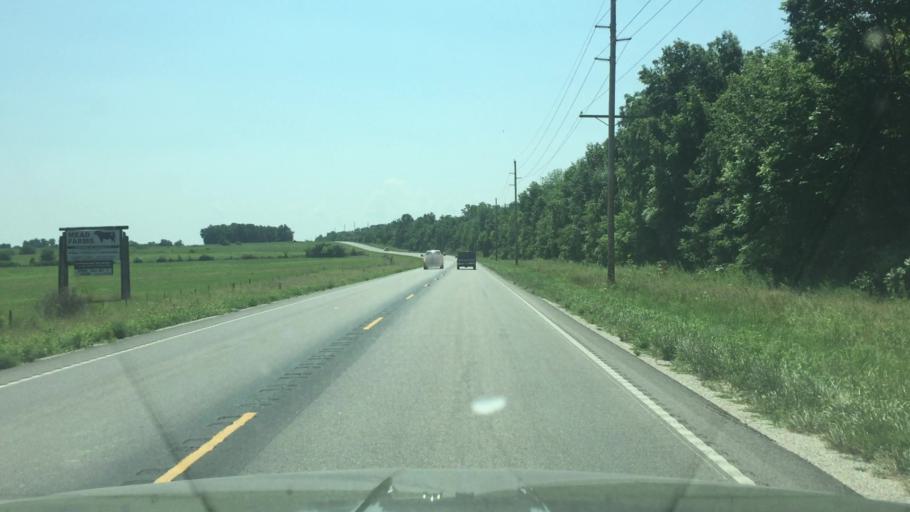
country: US
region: Missouri
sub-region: Miller County
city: Eldon
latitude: 38.3906
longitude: -92.7062
